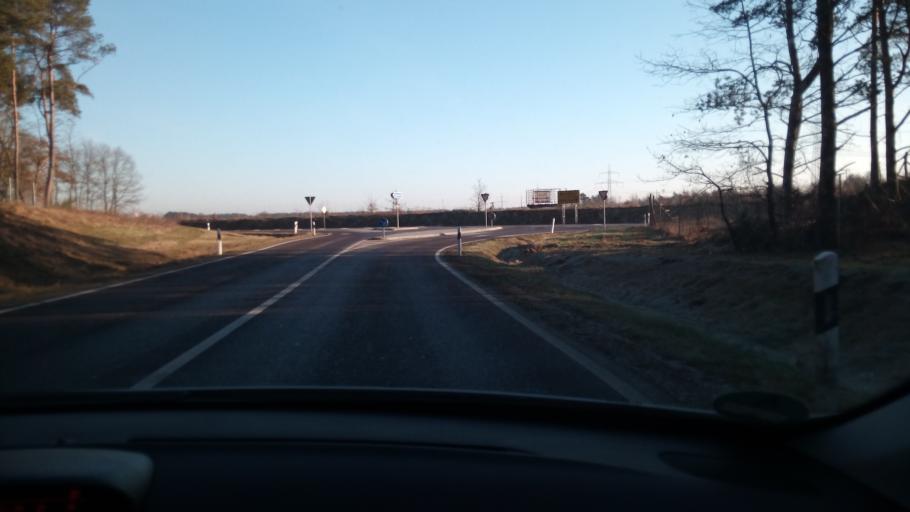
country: DE
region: Schleswig-Holstein
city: Besenthal
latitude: 53.5387
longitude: 10.7308
